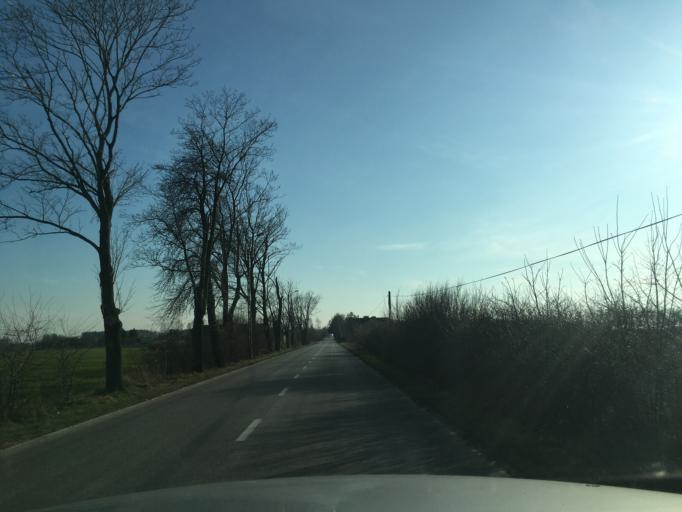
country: PL
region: Masovian Voivodeship
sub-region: Powiat pruszkowski
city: Nadarzyn
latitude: 52.0513
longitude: 20.8254
